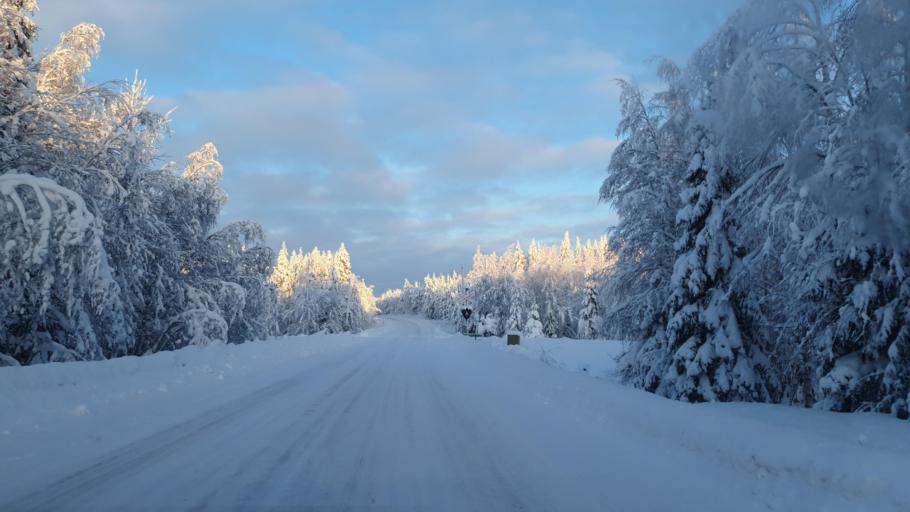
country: FI
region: Kainuu
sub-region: Kajaani
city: Vuokatti
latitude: 64.2562
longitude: 28.2351
